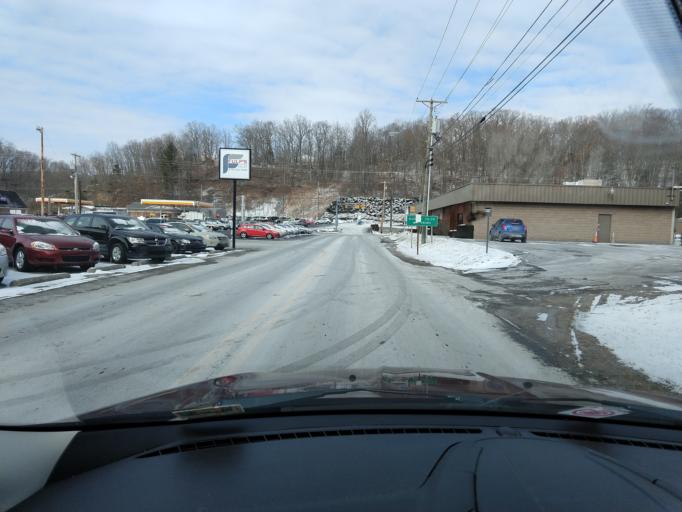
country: US
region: West Virginia
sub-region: Mercer County
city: Bluefield
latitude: 37.2459
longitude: -81.2411
